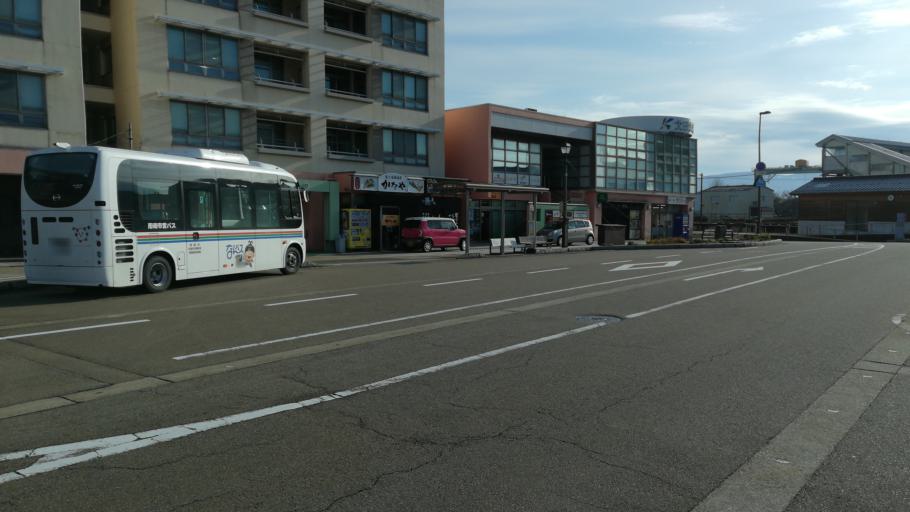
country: JP
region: Toyama
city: Nanto-shi
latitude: 36.5888
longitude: 136.9228
